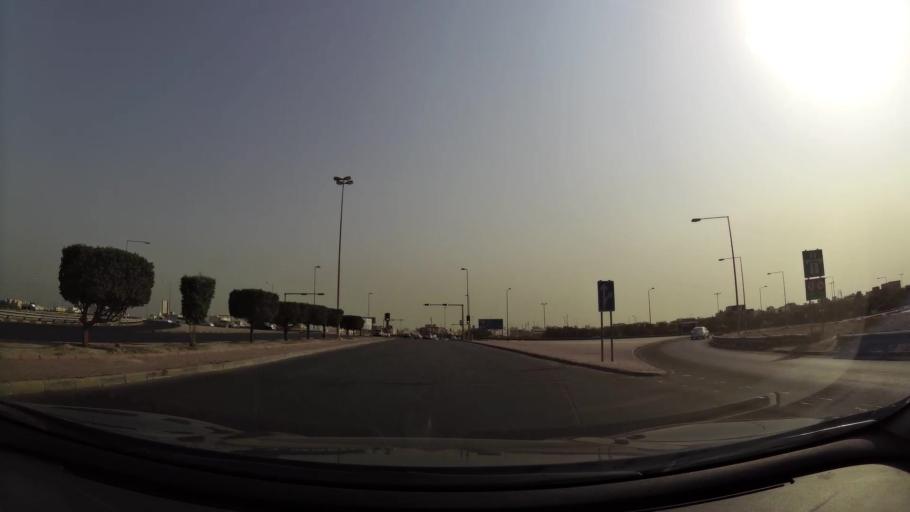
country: KW
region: Mubarak al Kabir
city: Sabah as Salim
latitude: 29.2659
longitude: 48.0666
